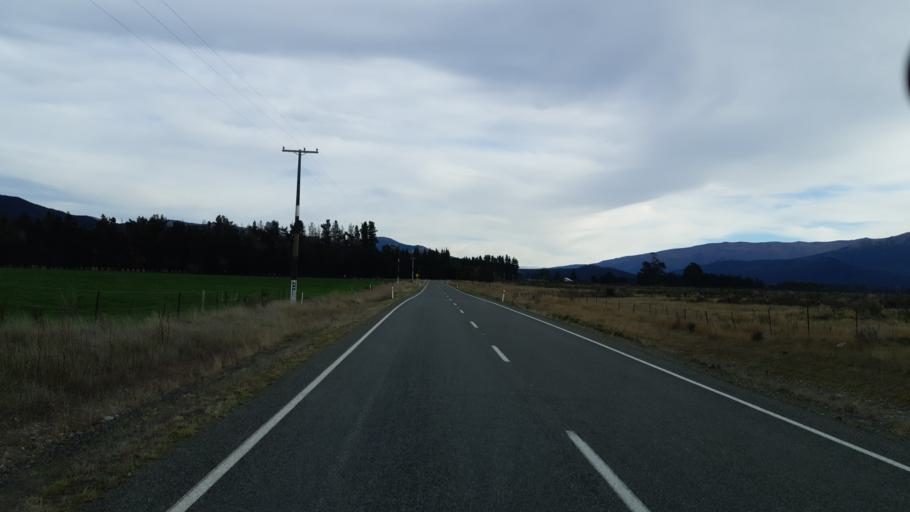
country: NZ
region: Tasman
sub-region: Tasman District
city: Brightwater
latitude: -41.6499
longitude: 173.2889
